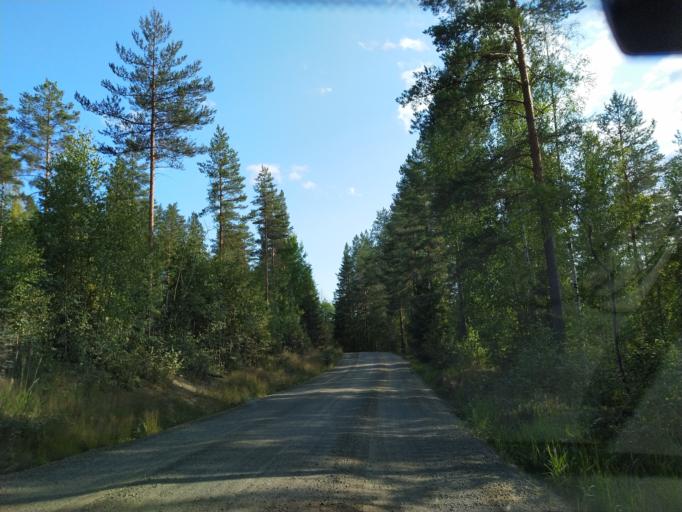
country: FI
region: Central Finland
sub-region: Jaemsae
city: Kuhmoinen
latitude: 61.7128
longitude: 24.9095
